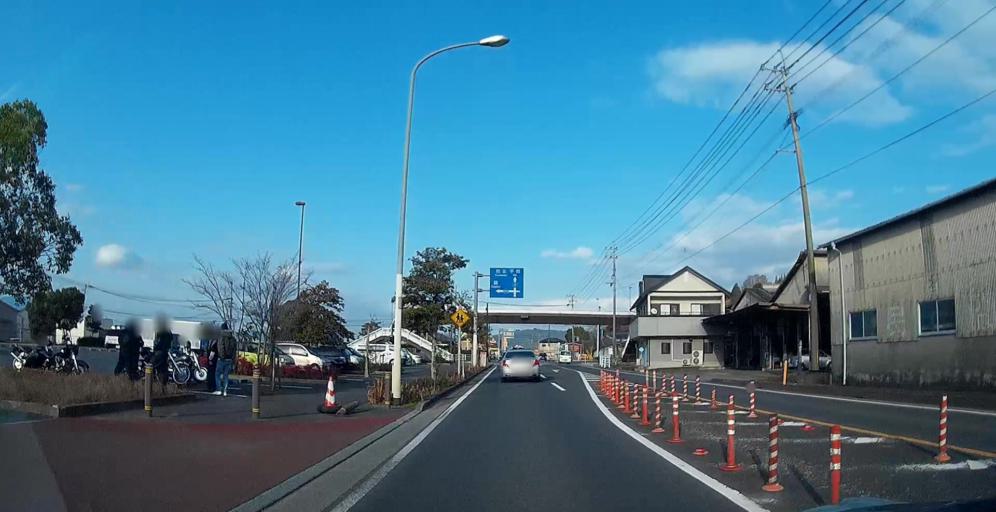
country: JP
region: Kumamoto
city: Matsubase
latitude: 32.5772
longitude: 130.6955
